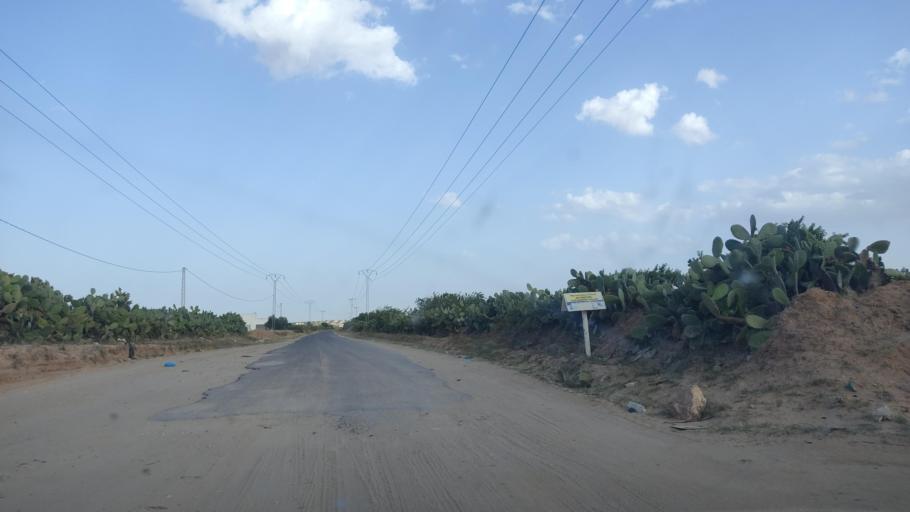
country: TN
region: Safaqis
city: Sfax
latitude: 34.8560
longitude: 10.6055
